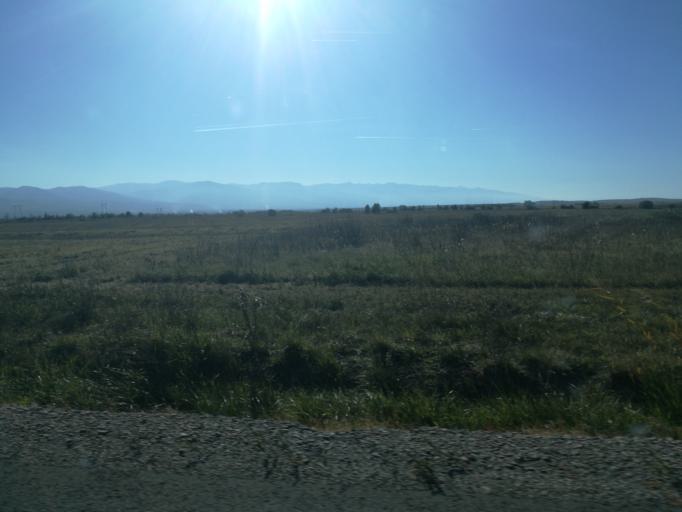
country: RO
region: Brasov
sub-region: Comuna Sinca Veche
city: Sinca Veche
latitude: 45.8035
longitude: 25.1757
